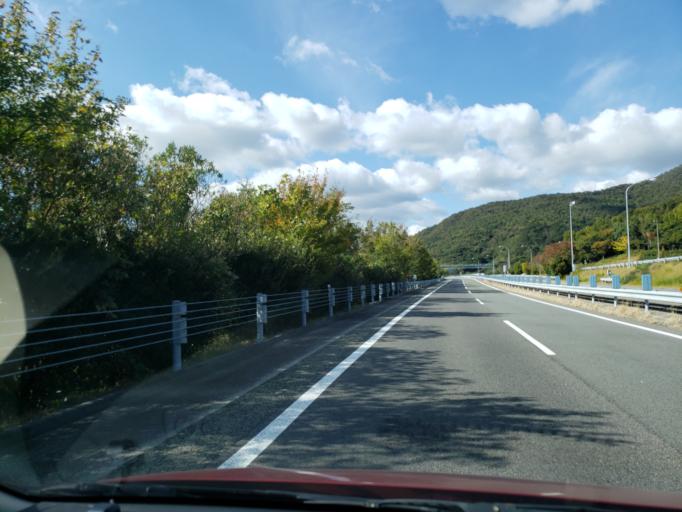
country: JP
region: Tokushima
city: Ishii
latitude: 34.1396
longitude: 134.4108
